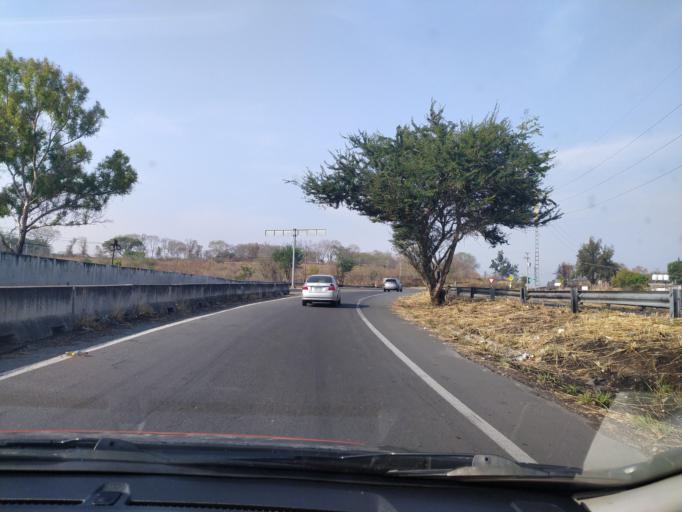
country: MX
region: Jalisco
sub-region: Acatlan de Juarez
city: Villa de los Ninos
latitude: 20.4277
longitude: -103.5808
